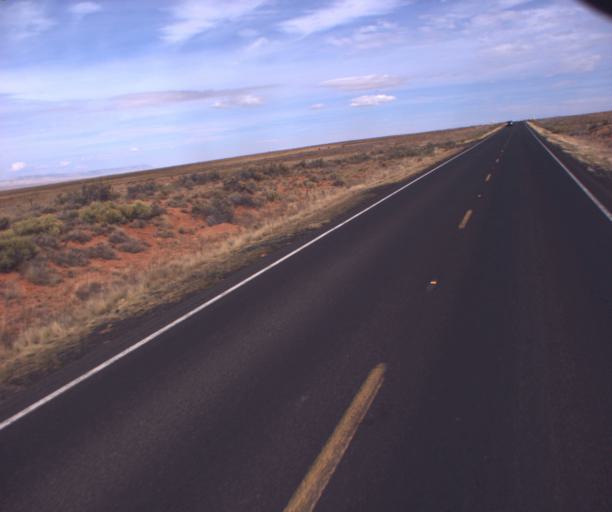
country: US
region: Arizona
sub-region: Apache County
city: Ganado
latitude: 35.8579
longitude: -109.5966
